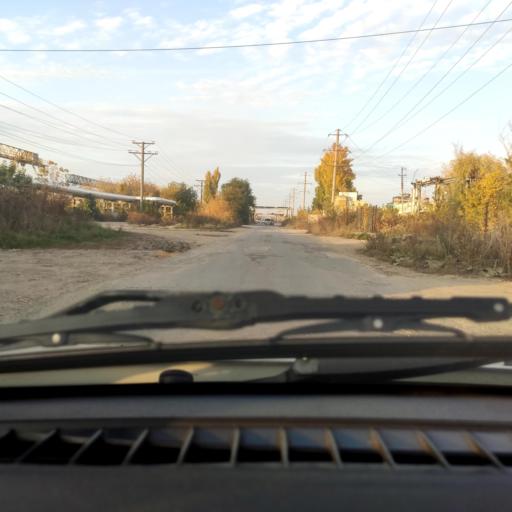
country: RU
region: Samara
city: Tol'yatti
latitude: 53.5284
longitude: 49.4611
